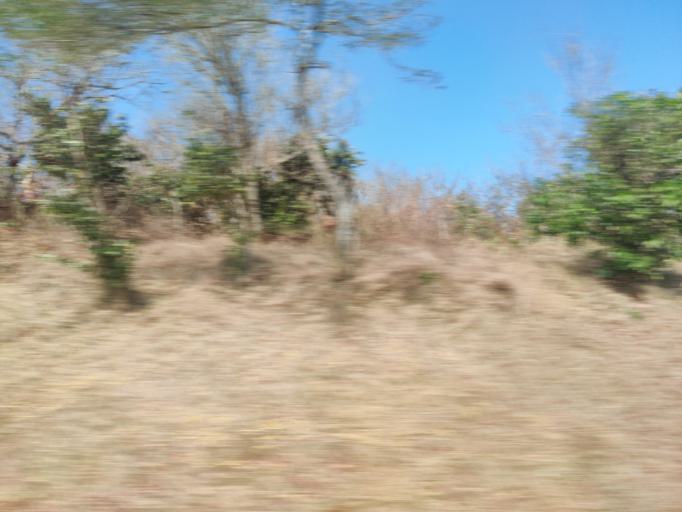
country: CO
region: Bolivar
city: Santa Catalina
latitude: 10.7442
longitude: -75.2530
